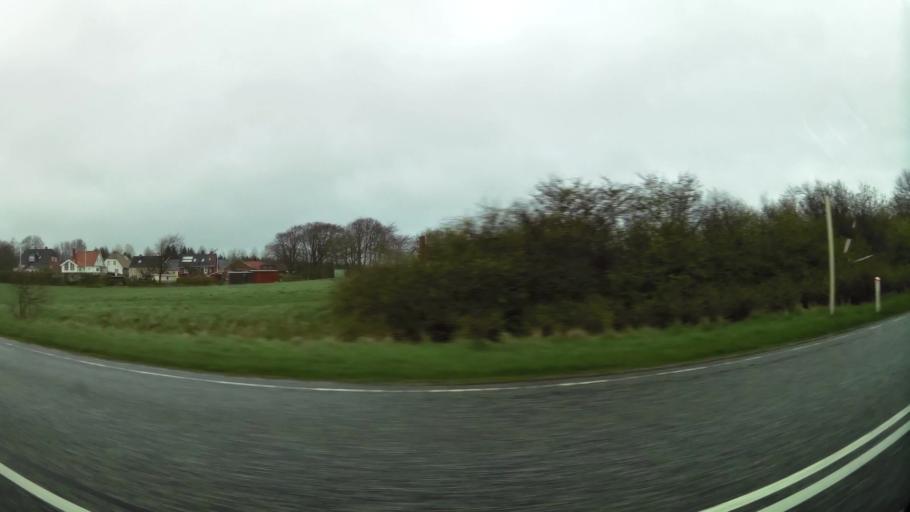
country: DK
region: Central Jutland
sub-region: Herning Kommune
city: Avlum
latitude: 56.2431
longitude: 8.8021
